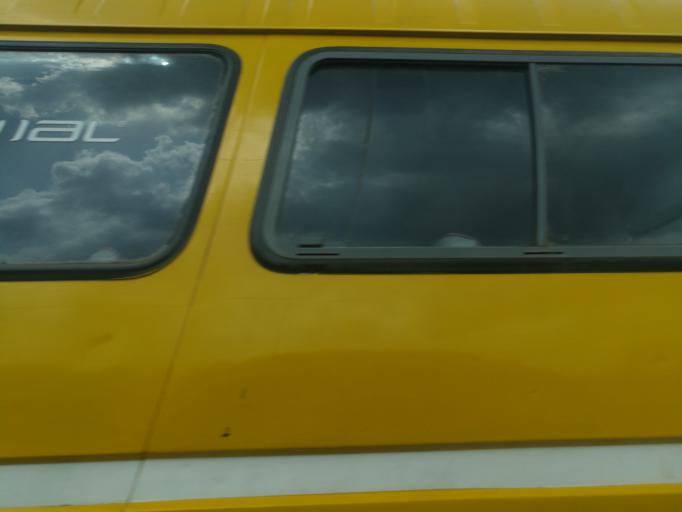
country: NG
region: Oyo
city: Ibadan
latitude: 7.4382
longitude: 3.9437
